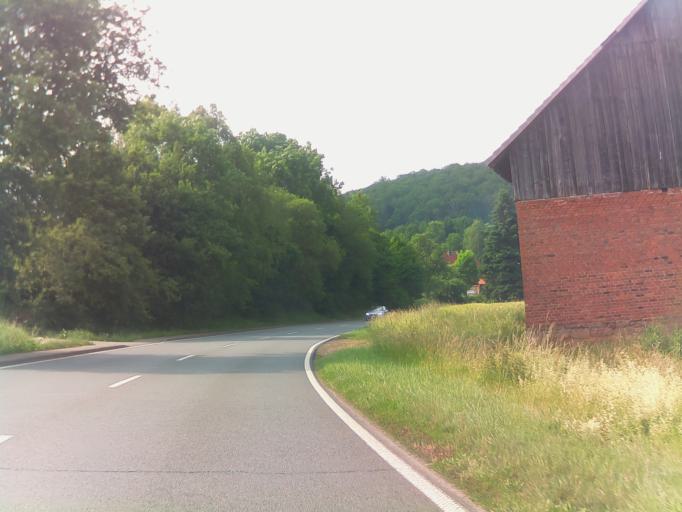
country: DE
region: Hesse
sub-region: Regierungsbezirk Kassel
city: Waldeck
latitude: 51.1827
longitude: 9.0843
